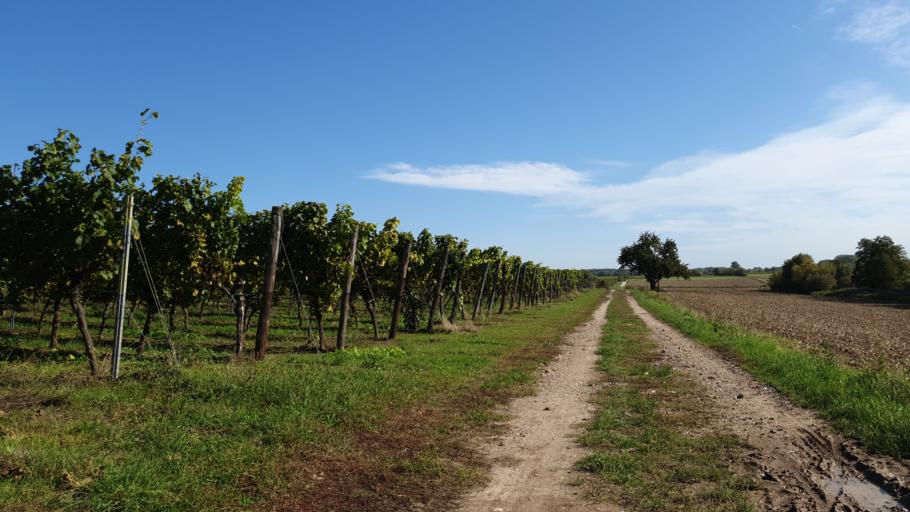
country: DE
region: Rheinland-Pfalz
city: Oberhausen
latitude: 49.1047
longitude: 8.0475
